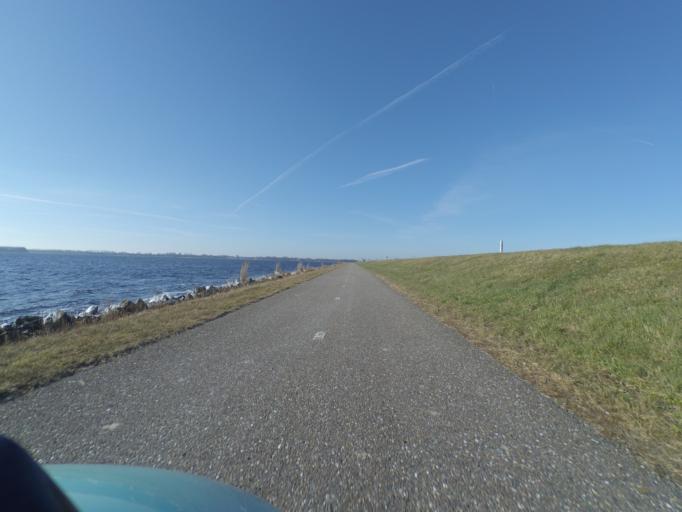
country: NL
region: North Holland
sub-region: Gemeente Naarden
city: Naarden
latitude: 52.3315
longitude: 5.1652
